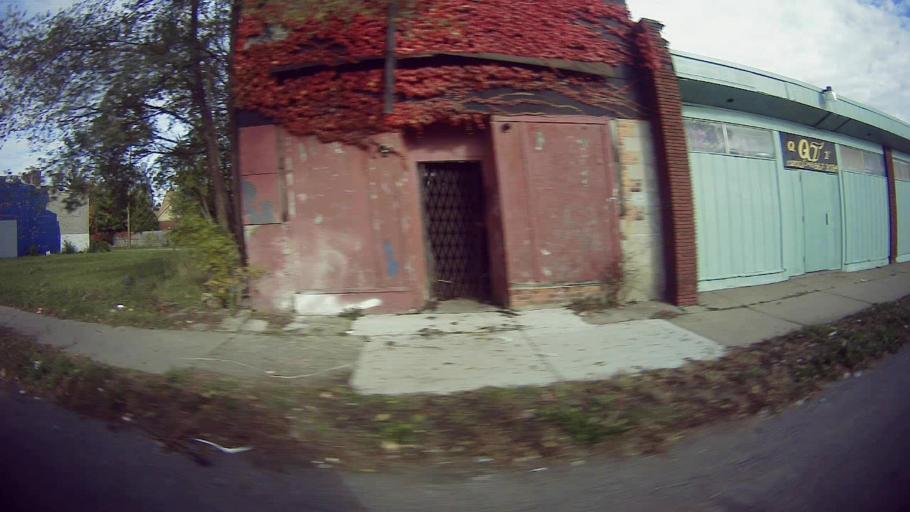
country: US
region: Michigan
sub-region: Oakland County
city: Oak Park
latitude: 42.4022
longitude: -83.1751
